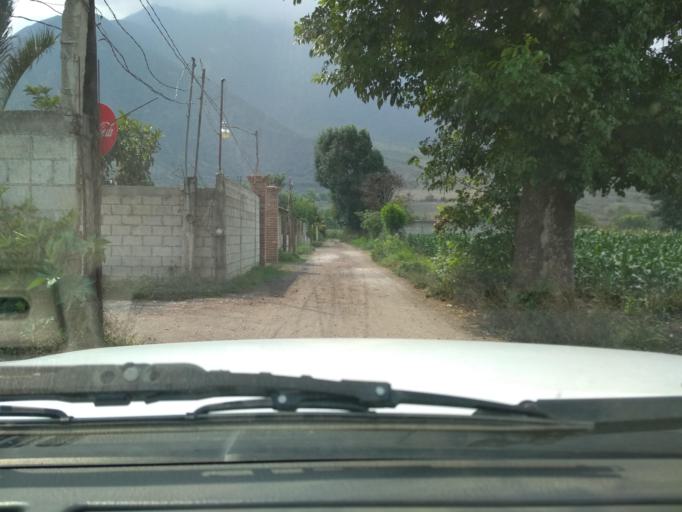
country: MX
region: Veracruz
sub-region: Acultzingo
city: Sierra de Agua
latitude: 18.7562
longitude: -97.2345
